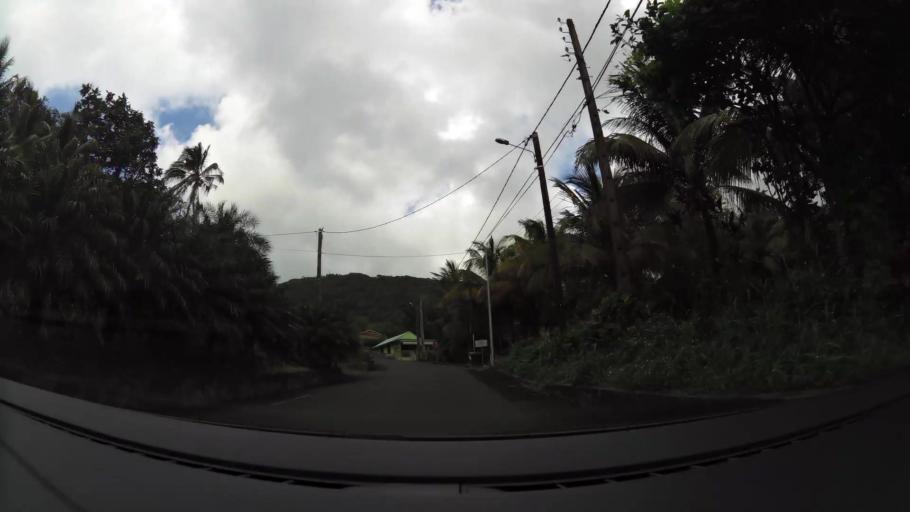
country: GP
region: Guadeloupe
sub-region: Guadeloupe
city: Trois-Rivieres
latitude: 15.9899
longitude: -61.6541
